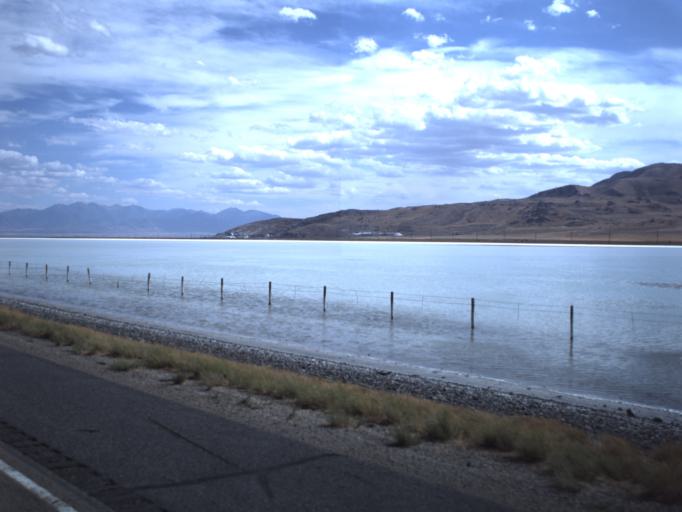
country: US
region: Utah
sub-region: Tooele County
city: Grantsville
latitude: 40.7366
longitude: -112.6123
